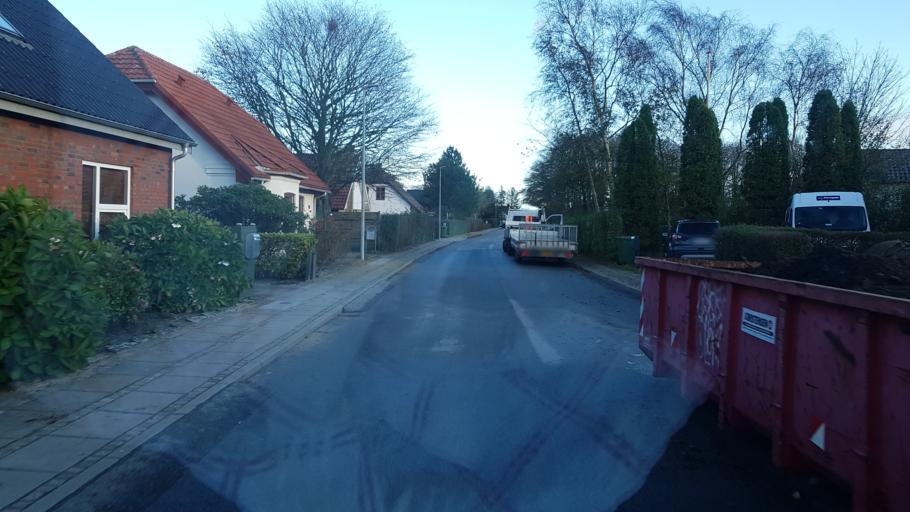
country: DK
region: South Denmark
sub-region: Vejen Kommune
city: Holsted
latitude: 55.4825
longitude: 8.9184
